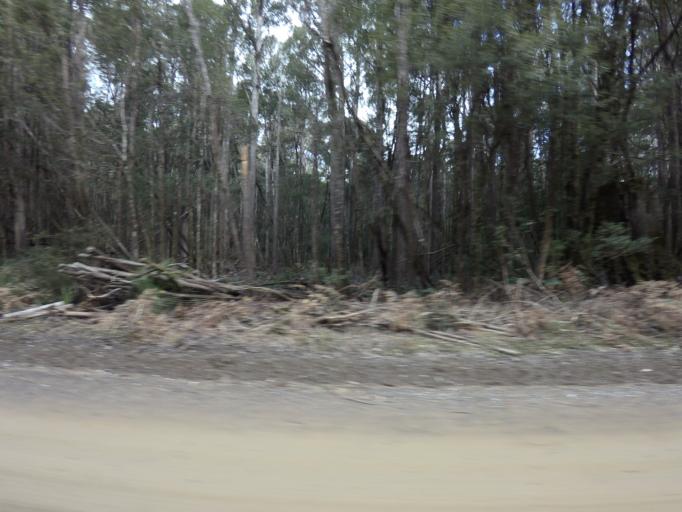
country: AU
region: Tasmania
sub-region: Huon Valley
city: Geeveston
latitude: -43.4031
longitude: 146.8651
